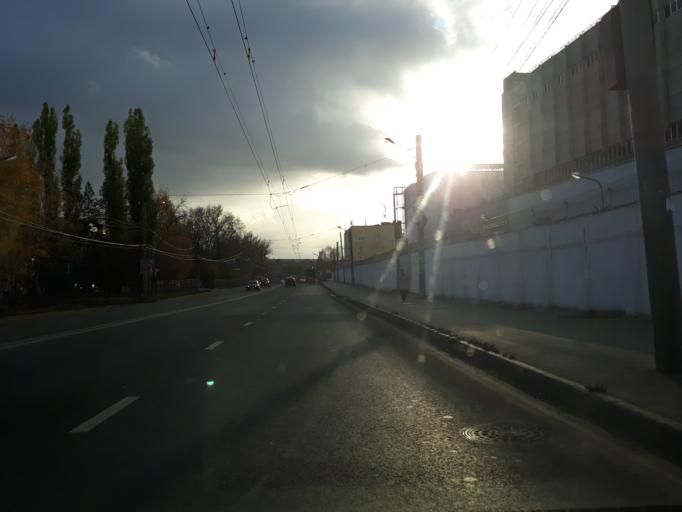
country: RU
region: Nizjnij Novgorod
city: Nizhniy Novgorod
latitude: 56.3187
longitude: 43.9042
